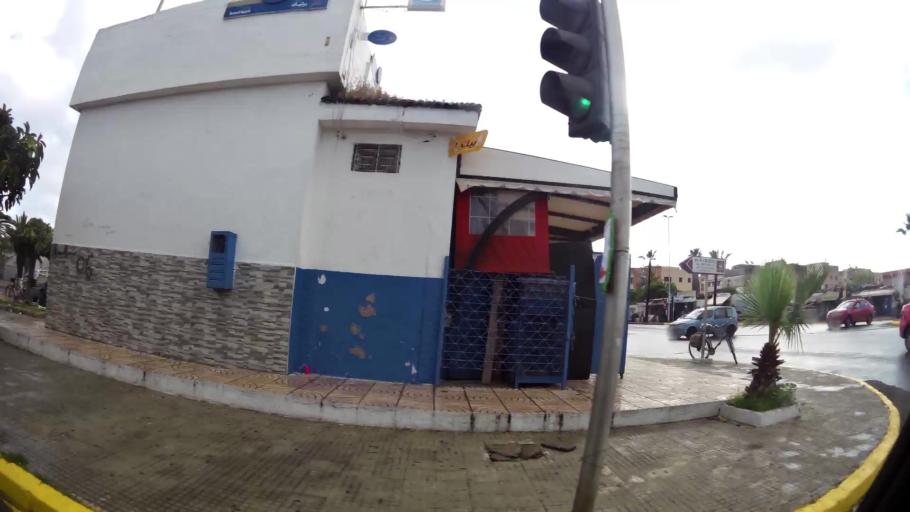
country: MA
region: Grand Casablanca
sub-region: Casablanca
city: Casablanca
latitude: 33.5584
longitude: -7.6800
